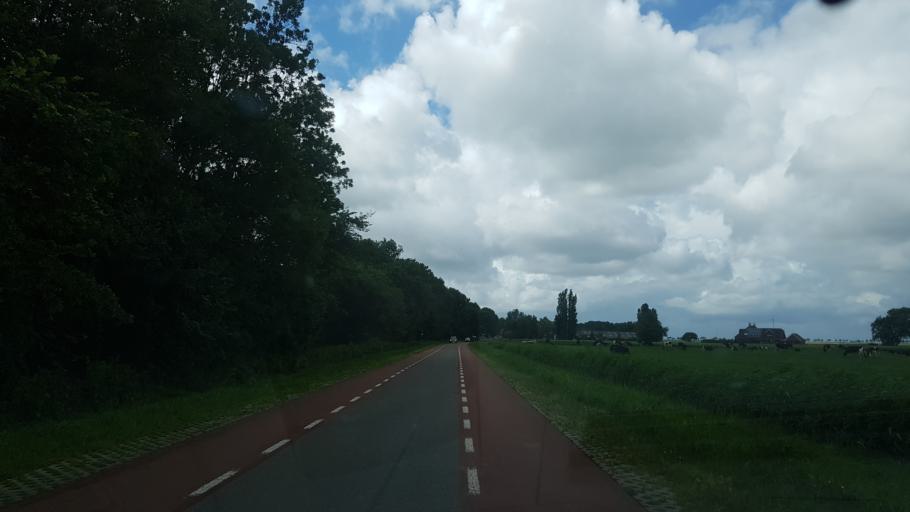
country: NL
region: Groningen
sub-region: Gemeente Winsum
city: Winsum
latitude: 53.3977
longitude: 6.4926
